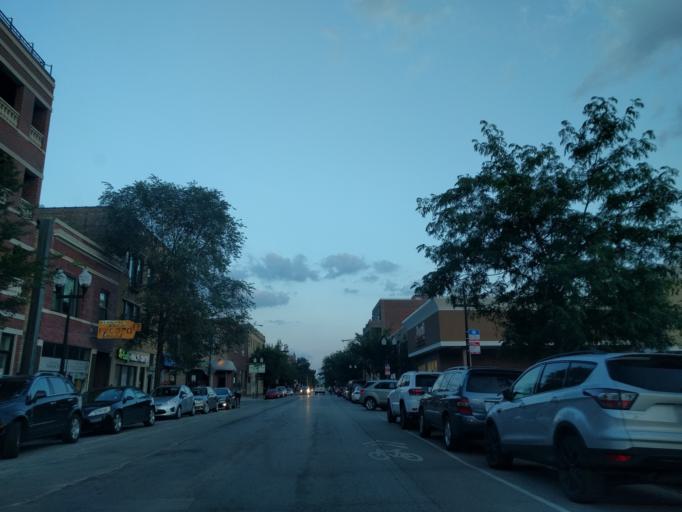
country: US
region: Illinois
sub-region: Cook County
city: Lincolnwood
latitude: 41.9591
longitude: -87.6822
